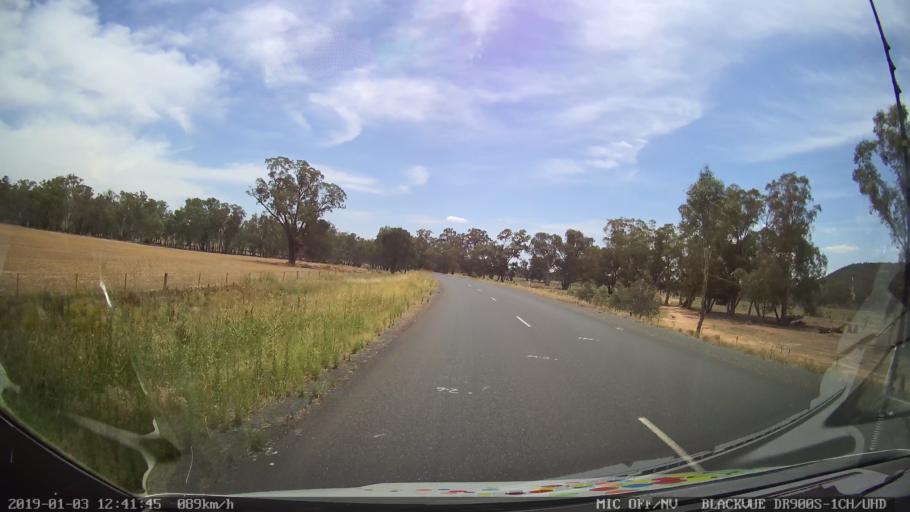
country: AU
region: New South Wales
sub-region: Weddin
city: Grenfell
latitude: -33.7955
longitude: 148.2154
